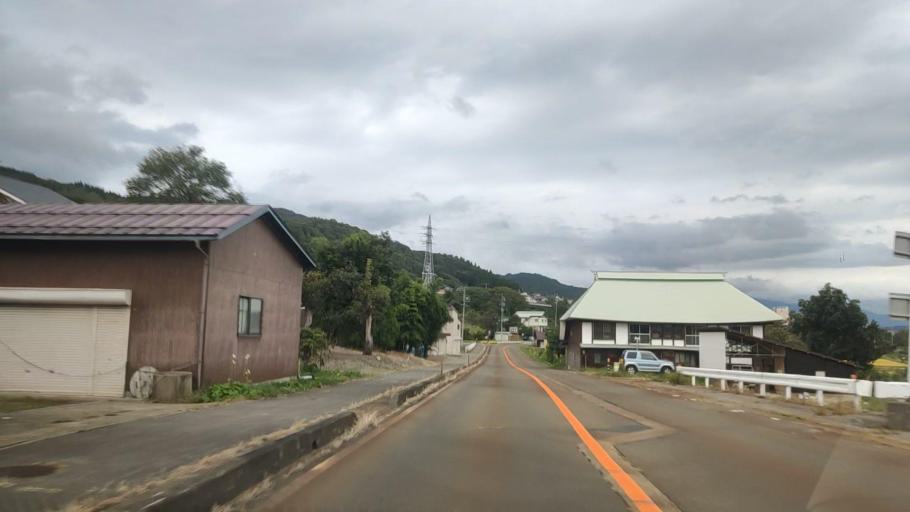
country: JP
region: Nagano
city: Iiyama
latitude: 36.8173
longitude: 138.3490
